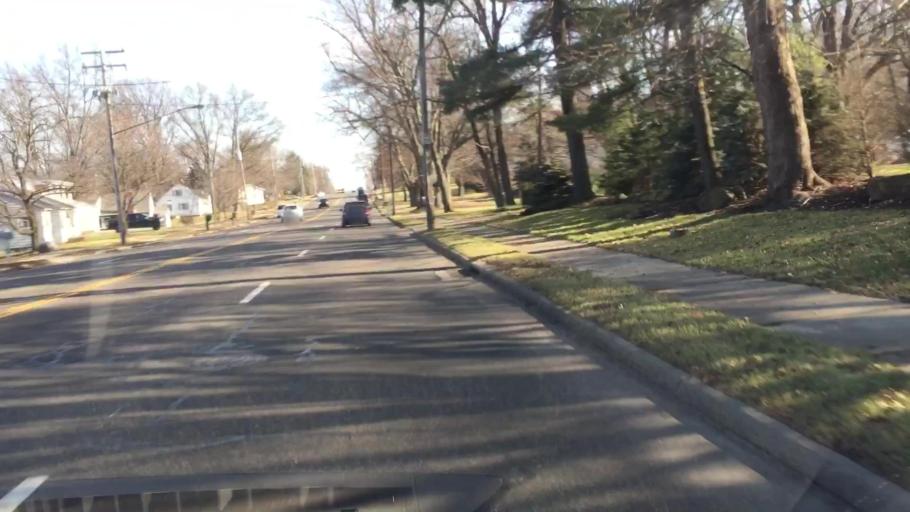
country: US
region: Ohio
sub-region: Summit County
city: Stow
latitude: 41.1590
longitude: -81.4240
